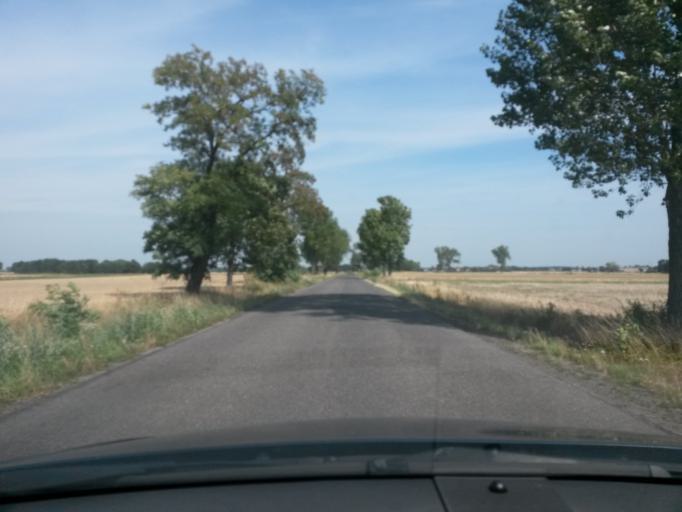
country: PL
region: Lower Silesian Voivodeship
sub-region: Powiat legnicki
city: Prochowice
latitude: 51.2006
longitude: 16.3464
